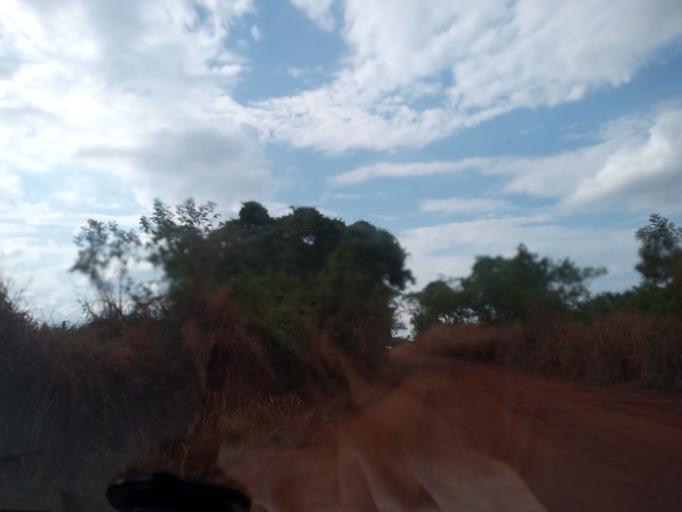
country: BR
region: Minas Gerais
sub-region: Ituiutaba
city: Ituiutaba
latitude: -19.1879
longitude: -49.5120
